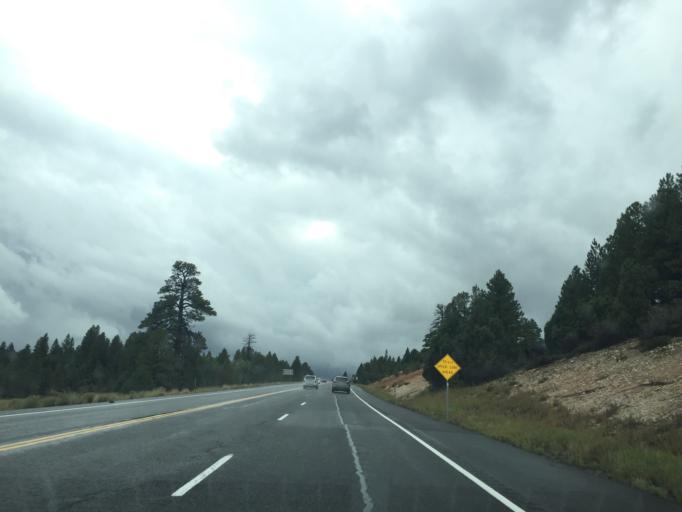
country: US
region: Utah
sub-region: Garfield County
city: Panguitch
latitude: 37.4945
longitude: -112.5090
